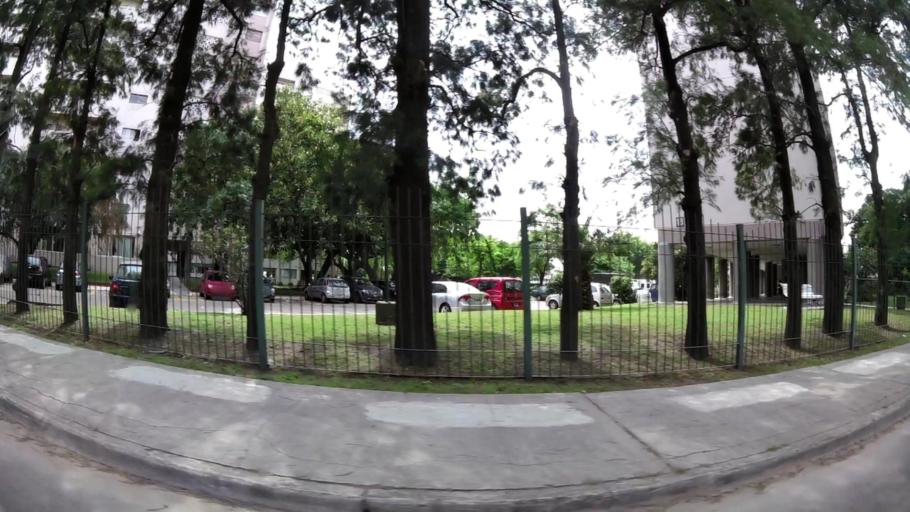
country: AR
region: Buenos Aires F.D.
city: Villa Lugano
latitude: -34.7084
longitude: -58.5047
